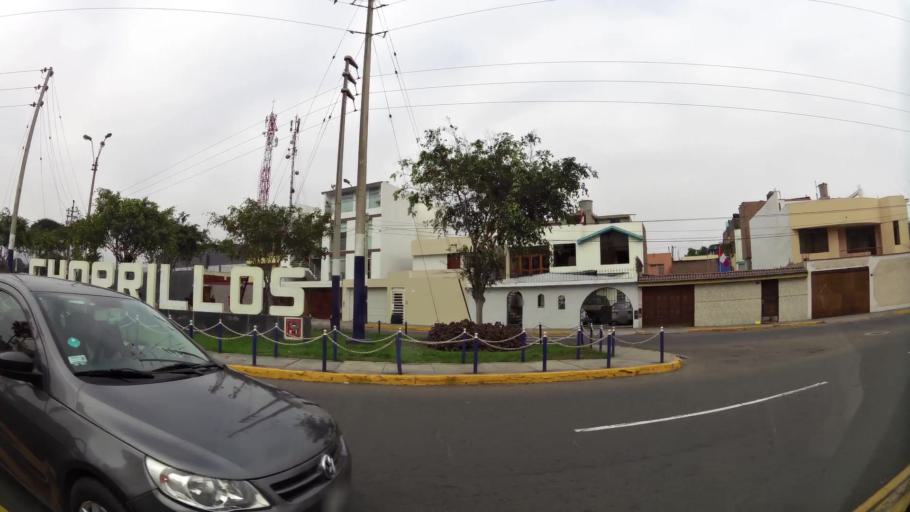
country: PE
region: Lima
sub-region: Lima
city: Surco
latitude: -12.1713
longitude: -77.0186
